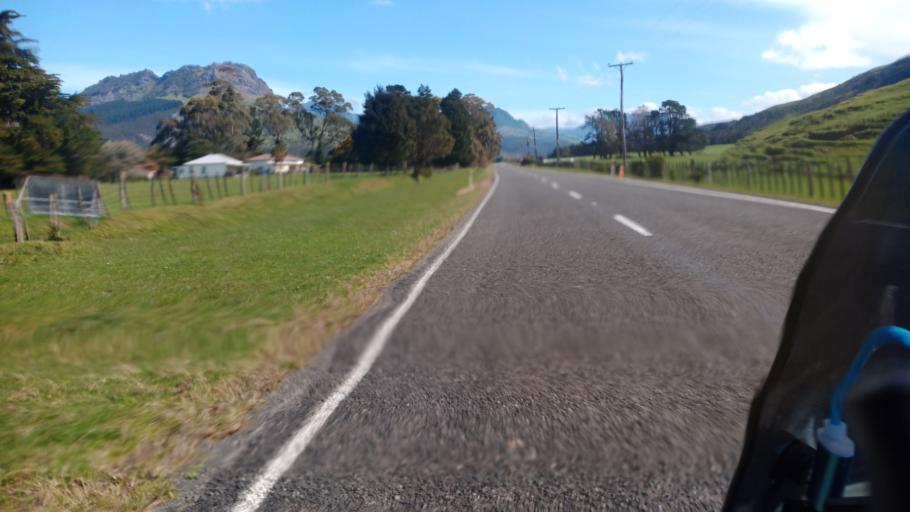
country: NZ
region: Gisborne
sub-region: Gisborne District
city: Gisborne
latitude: -37.8640
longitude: 178.2283
